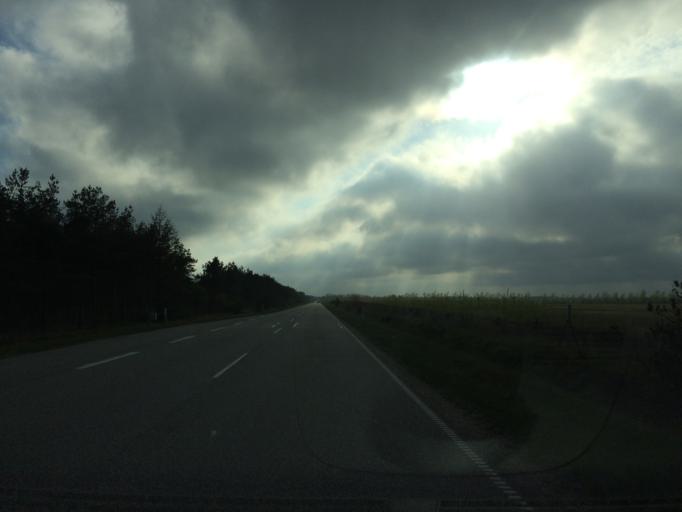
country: DK
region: Central Jutland
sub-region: Viborg Kommune
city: Karup
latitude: 56.3377
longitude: 9.0510
